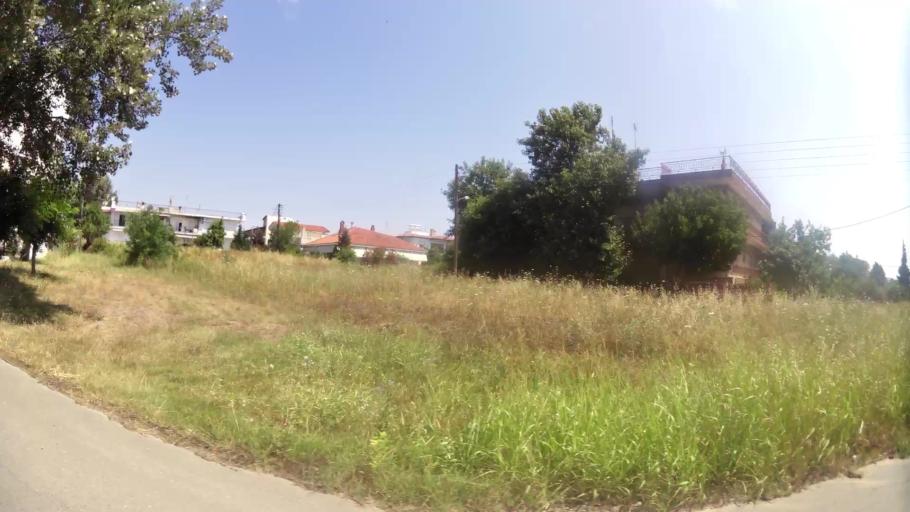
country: GR
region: Central Macedonia
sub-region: Nomos Thessalonikis
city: Nea Michaniona
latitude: 40.4955
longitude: 22.8199
